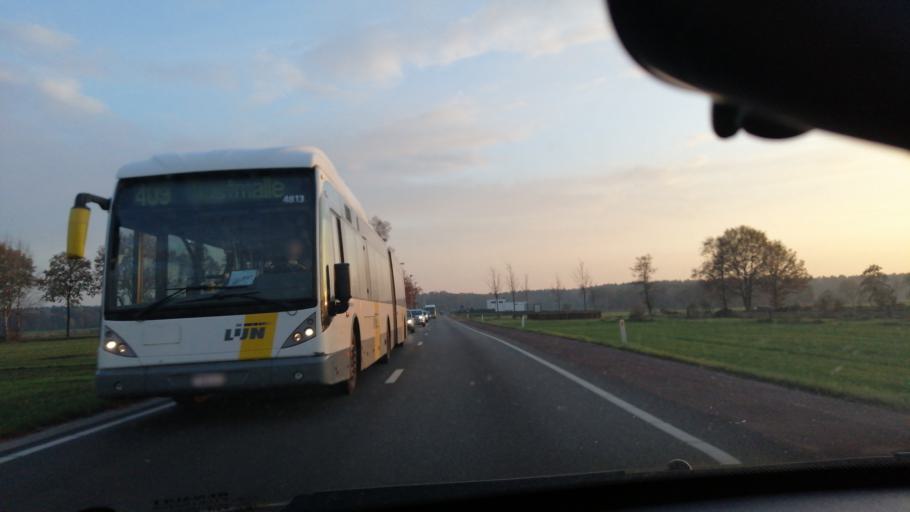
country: BE
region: Flanders
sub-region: Provincie Antwerpen
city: Lille
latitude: 51.2085
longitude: 4.8180
